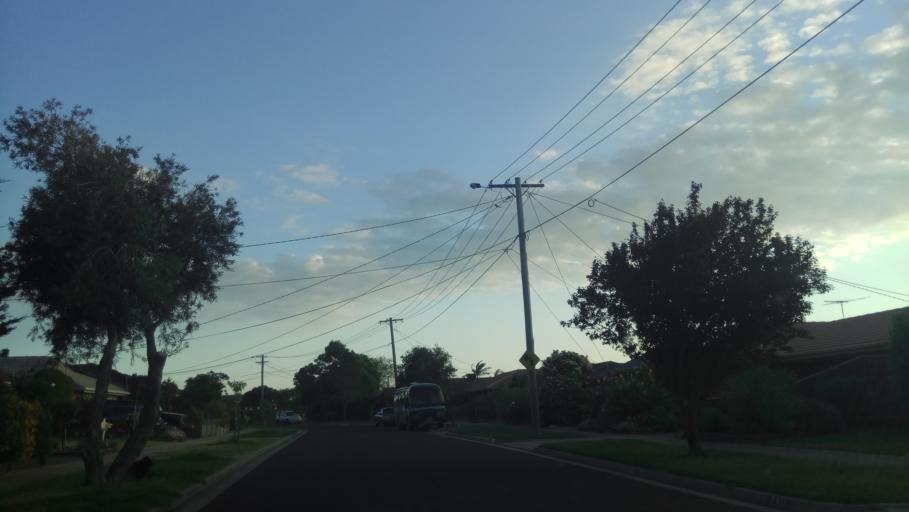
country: AU
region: Victoria
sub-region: Hobsons Bay
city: Altona Meadows
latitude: -37.8792
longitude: 144.7883
